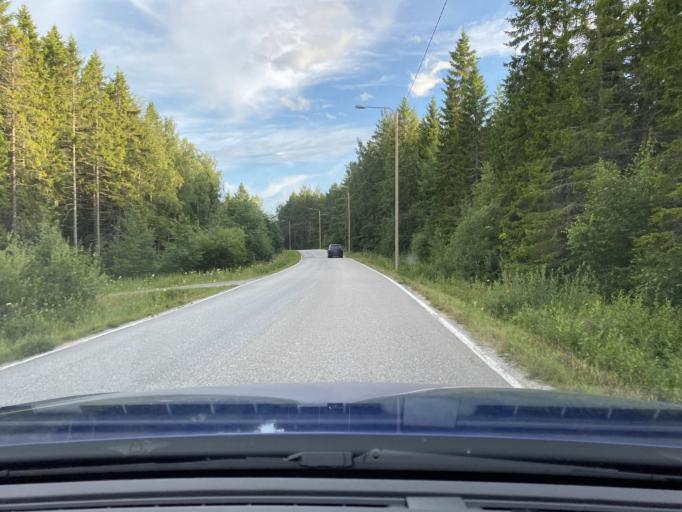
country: FI
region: Ostrobothnia
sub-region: Vaasa
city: Korsnaes
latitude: 62.9537
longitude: 21.1772
